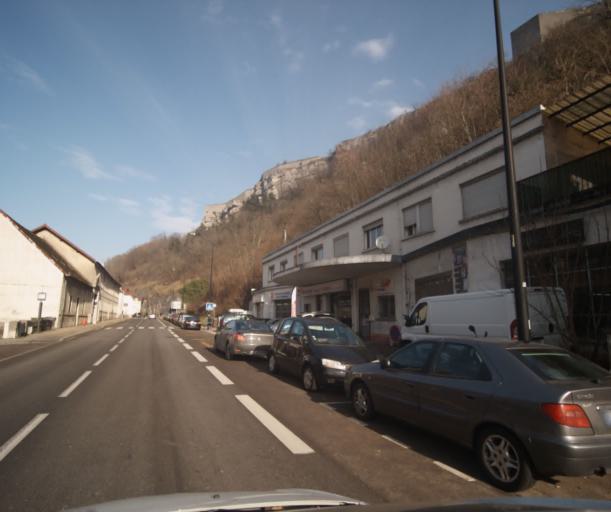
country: FR
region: Franche-Comte
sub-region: Departement du Doubs
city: Besancon
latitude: 47.2286
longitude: 6.0317
